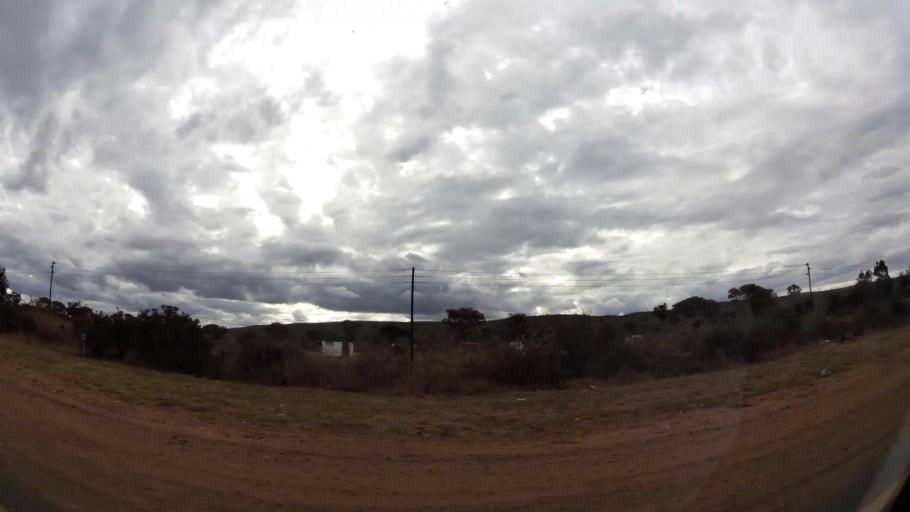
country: ZA
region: Limpopo
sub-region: Waterberg District Municipality
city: Modimolle
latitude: -24.6795
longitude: 28.4359
